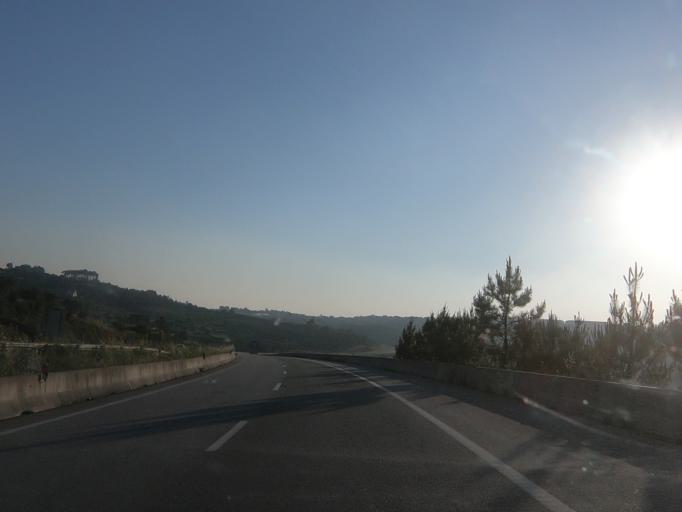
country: PT
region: Guarda
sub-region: Celorico da Beira
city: Celorico da Beira
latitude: 40.6280
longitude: -7.3736
